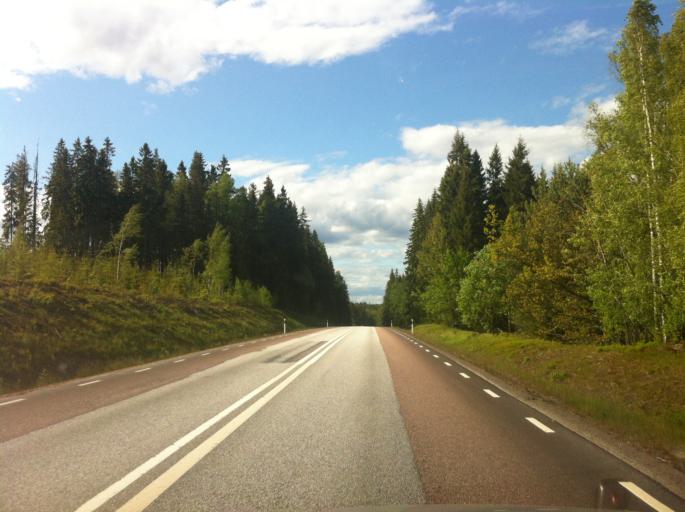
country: SE
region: Vaermland
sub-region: Storfors Kommun
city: Storfors
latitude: 59.4861
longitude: 14.2569
